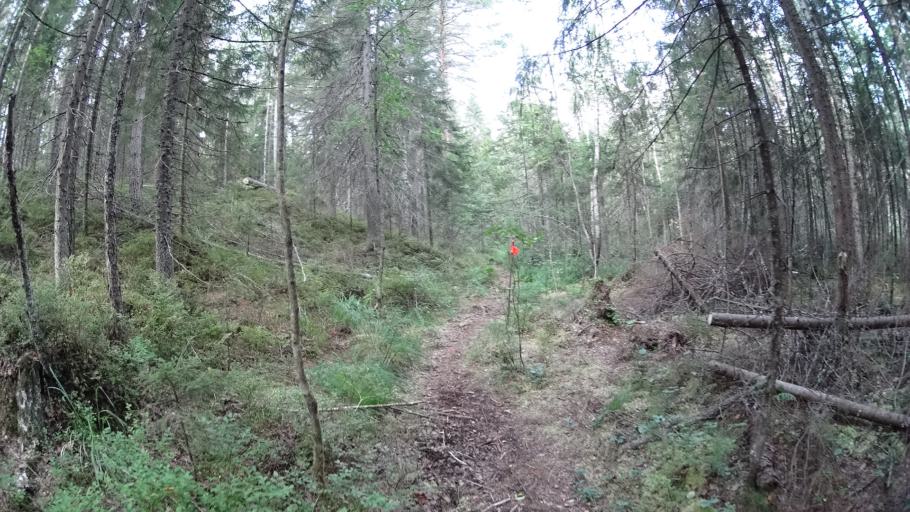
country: FI
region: Uusimaa
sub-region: Helsinki
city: Espoo
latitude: 60.2987
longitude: 24.5844
